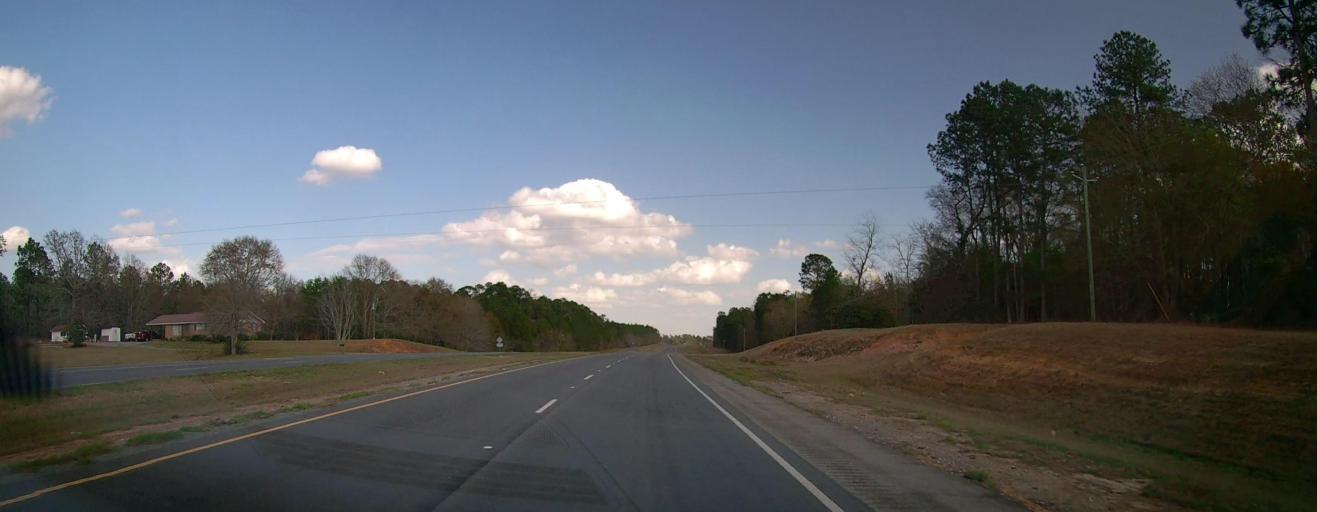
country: US
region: Georgia
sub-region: Telfair County
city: Helena
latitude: 32.1052
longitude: -82.9756
